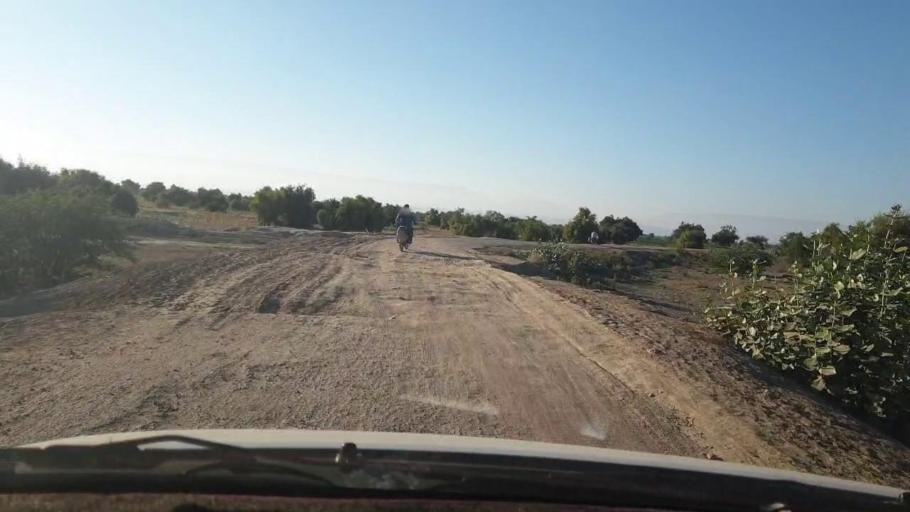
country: PK
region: Sindh
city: Johi
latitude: 26.7603
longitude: 67.4691
